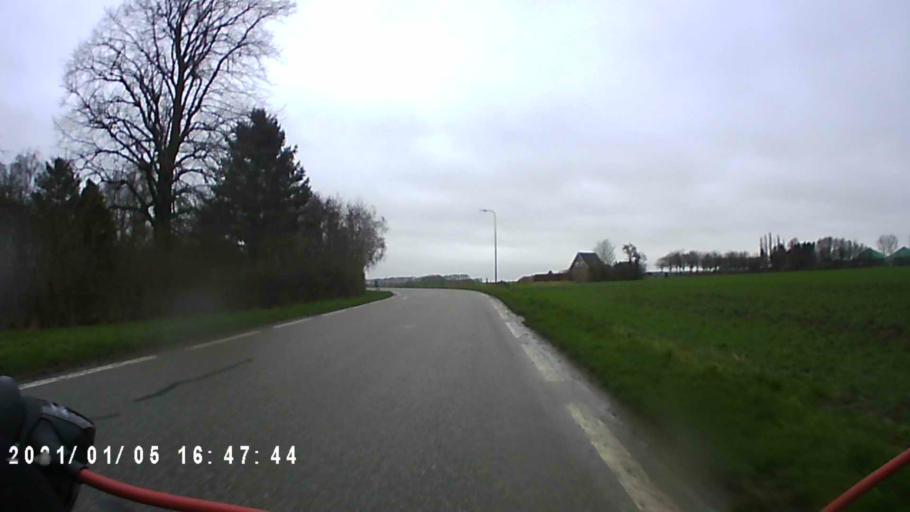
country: NL
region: Groningen
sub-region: Gemeente  Oldambt
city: Winschoten
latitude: 53.2266
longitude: 7.0535
